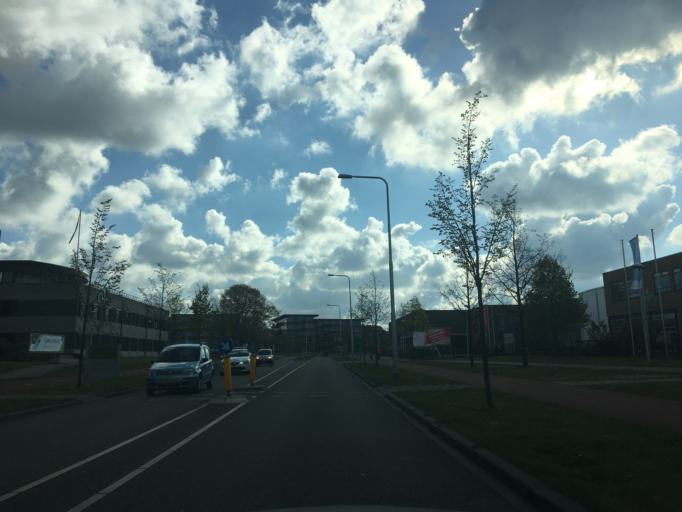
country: NL
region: Gelderland
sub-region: Gemeente Ede
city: Ede
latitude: 52.0188
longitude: 5.6629
